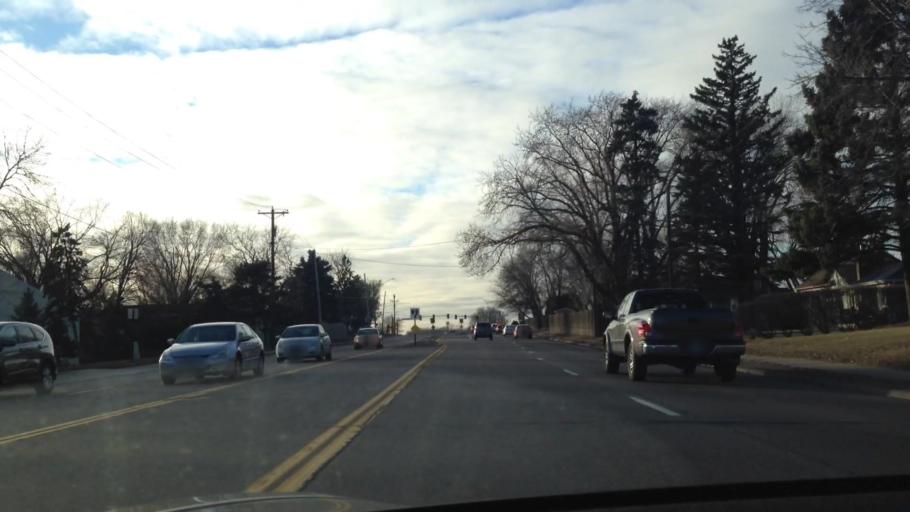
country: US
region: Minnesota
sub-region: Hennepin County
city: New Hope
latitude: 45.0334
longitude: -93.3921
